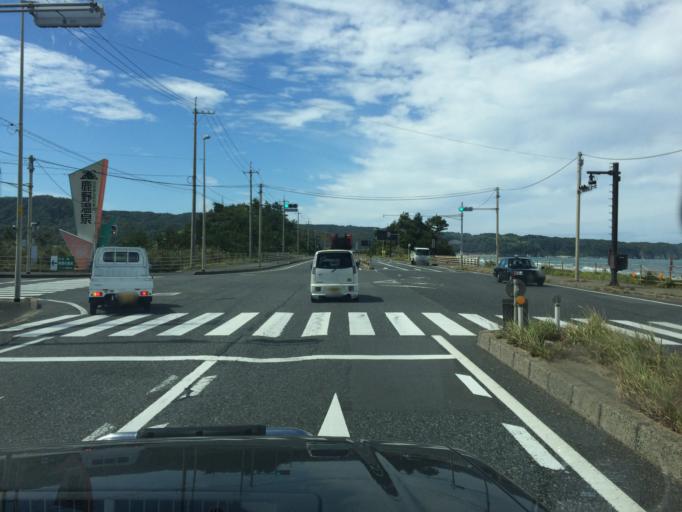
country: JP
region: Tottori
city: Tottori
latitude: 35.5179
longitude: 134.0461
